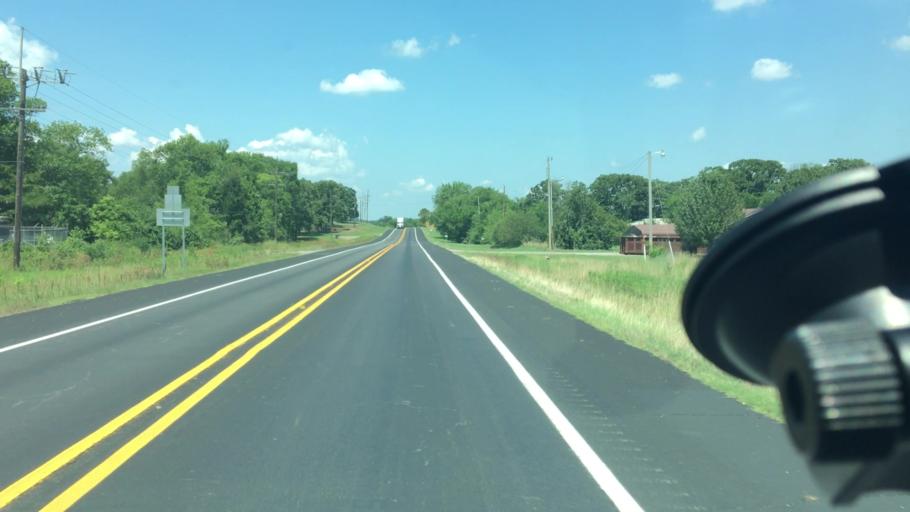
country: US
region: Arkansas
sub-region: Sebastian County
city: Lavaca
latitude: 35.3026
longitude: -94.1642
